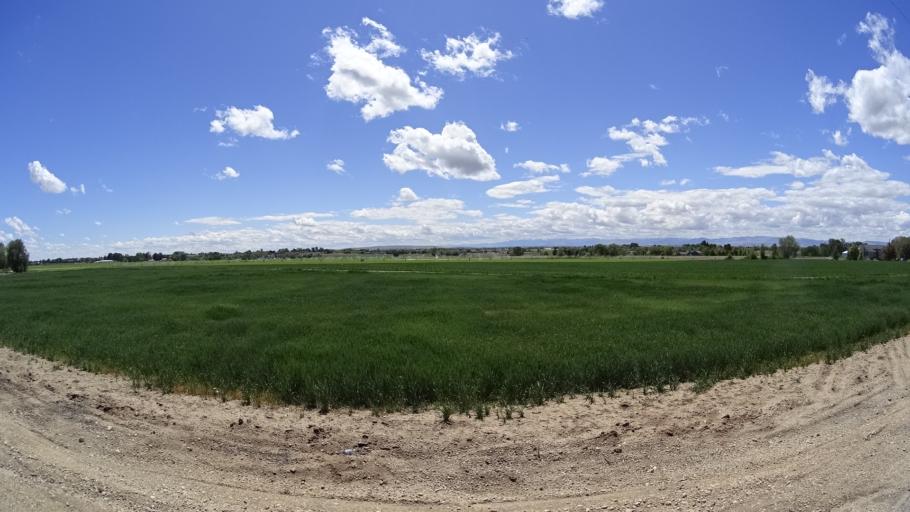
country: US
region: Idaho
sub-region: Ada County
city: Meridian
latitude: 43.5903
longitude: -116.4667
